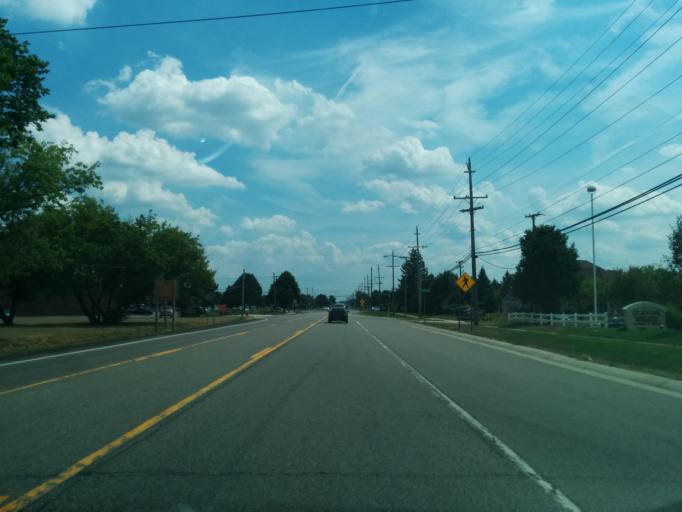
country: US
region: Michigan
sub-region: Oakland County
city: Novi
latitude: 42.4746
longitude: -83.4480
